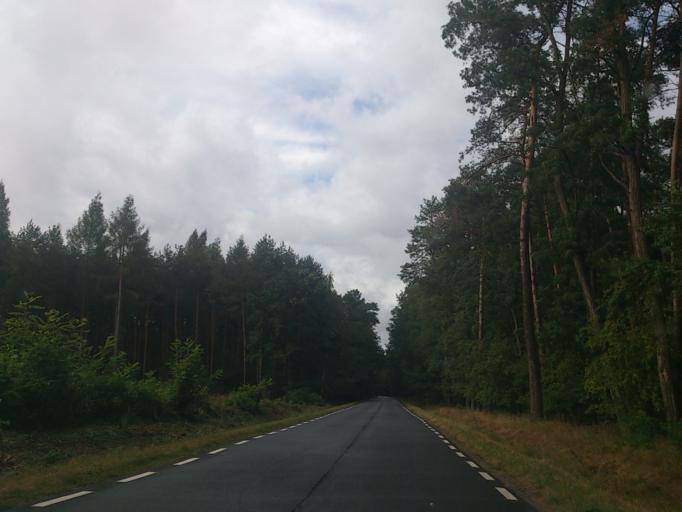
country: PL
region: Greater Poland Voivodeship
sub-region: Powiat poznanski
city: Pobiedziska
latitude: 52.5113
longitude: 17.2008
